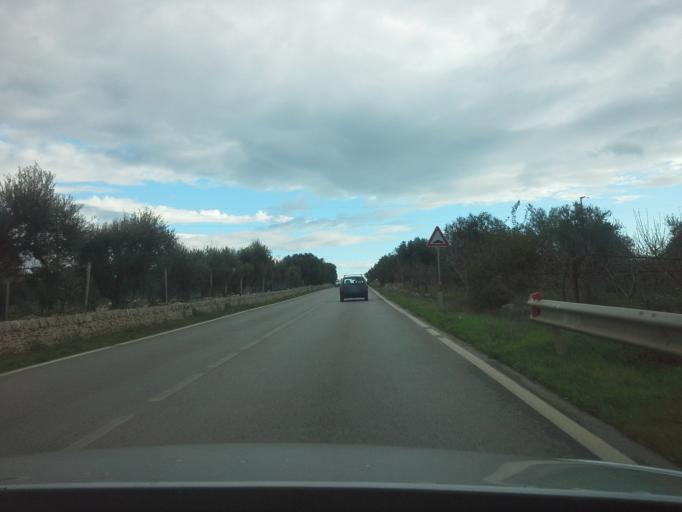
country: IT
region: Apulia
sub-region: Provincia di Bari
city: Turi
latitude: 40.8854
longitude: 17.0529
